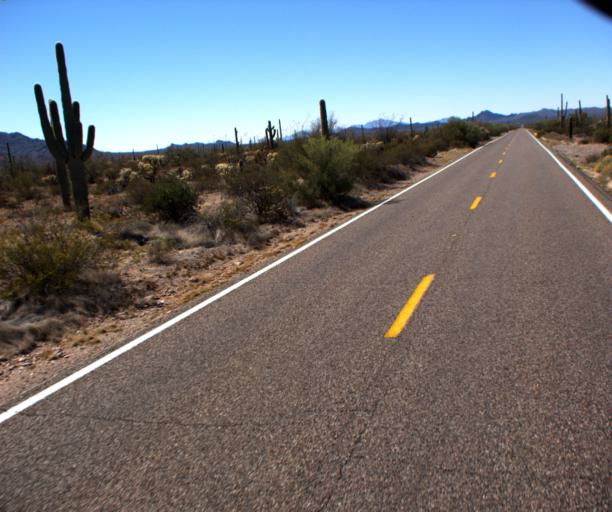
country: MX
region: Sonora
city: Sonoyta
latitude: 32.0738
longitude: -112.7819
